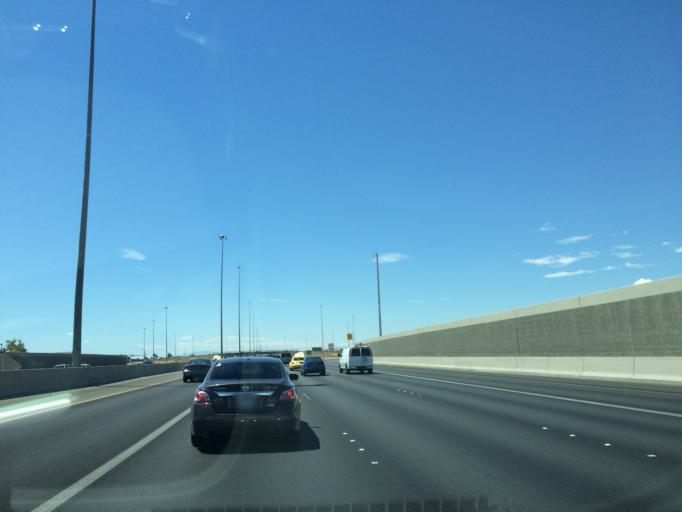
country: US
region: Nevada
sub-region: Clark County
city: Las Vegas
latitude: 36.2461
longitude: -115.2469
